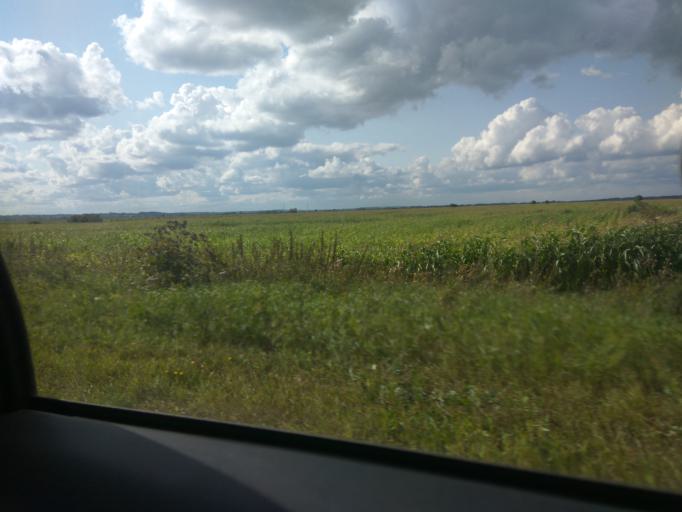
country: RU
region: Moskovskaya
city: Ramenskoye
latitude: 55.5077
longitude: 38.2538
